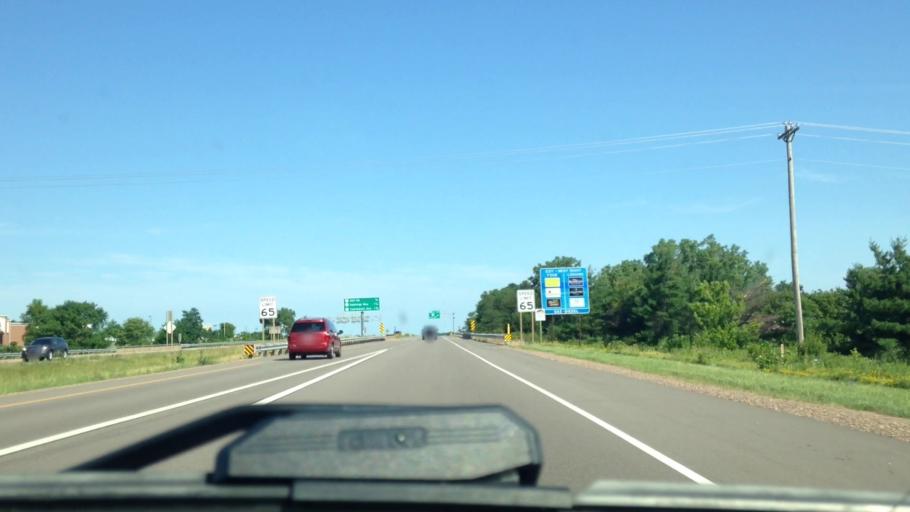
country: US
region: Wisconsin
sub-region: Eau Claire County
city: Altoona
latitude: 44.7711
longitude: -91.4261
